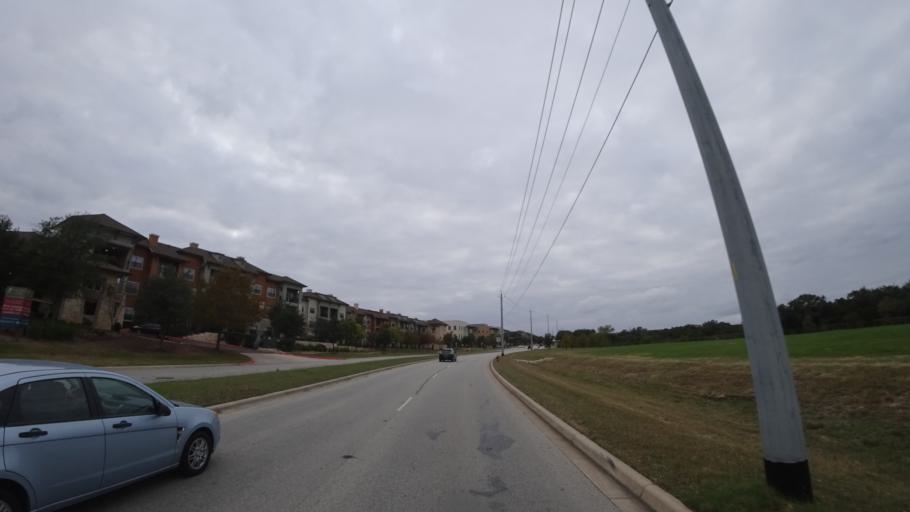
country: US
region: Texas
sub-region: Travis County
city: Bee Cave
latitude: 30.3102
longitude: -97.9365
